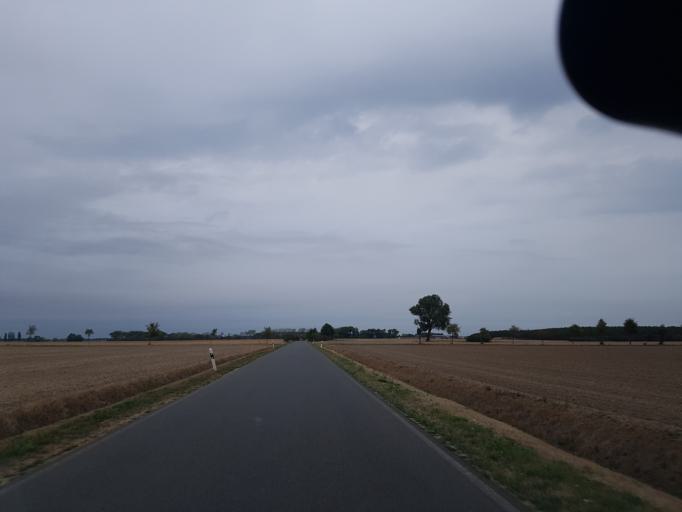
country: DE
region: Saxony-Anhalt
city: Prettin
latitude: 51.7167
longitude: 12.8923
